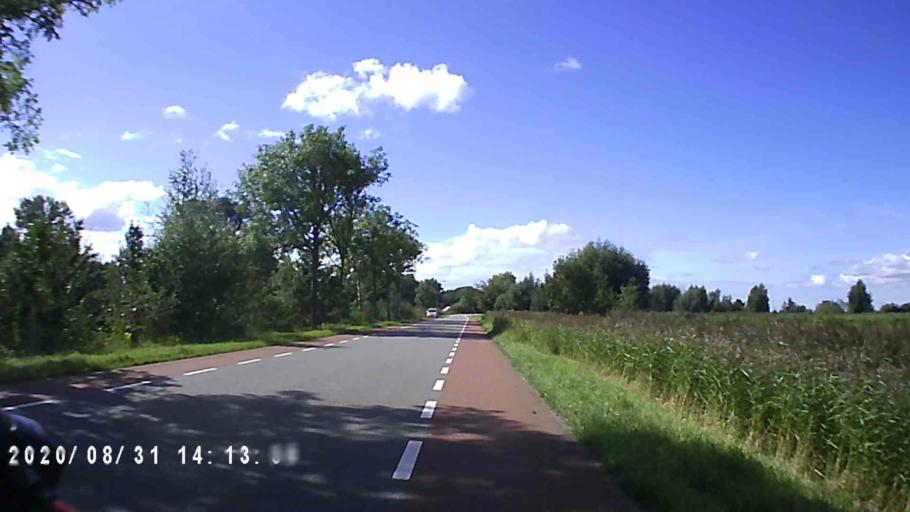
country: NL
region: Groningen
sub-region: Gemeente Zuidhorn
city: Aduard
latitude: 53.2081
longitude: 6.4678
